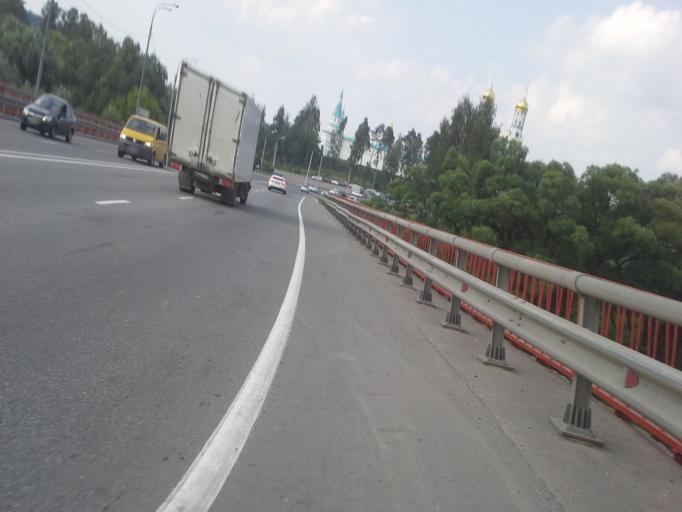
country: RU
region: Moskovskaya
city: Istra
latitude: 55.9173
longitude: 36.8430
